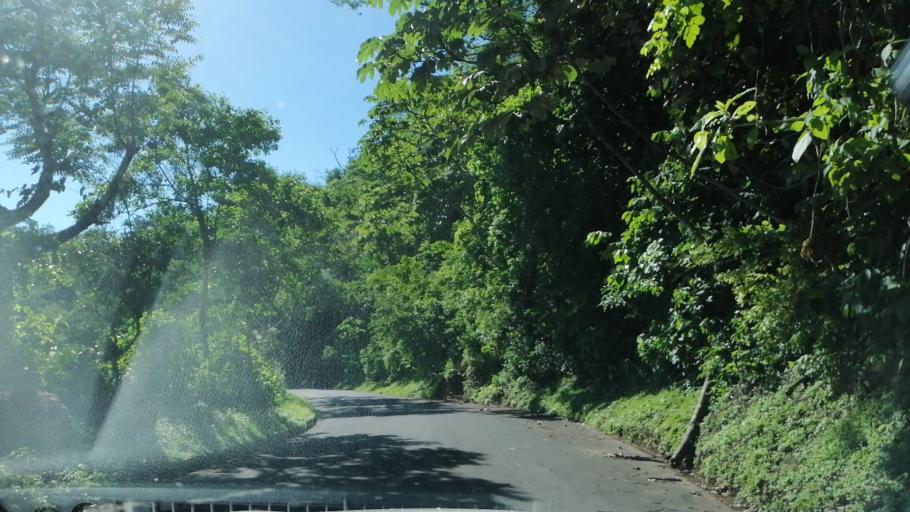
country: SV
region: Morazan
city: Cacaopera
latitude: 13.7865
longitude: -88.0317
